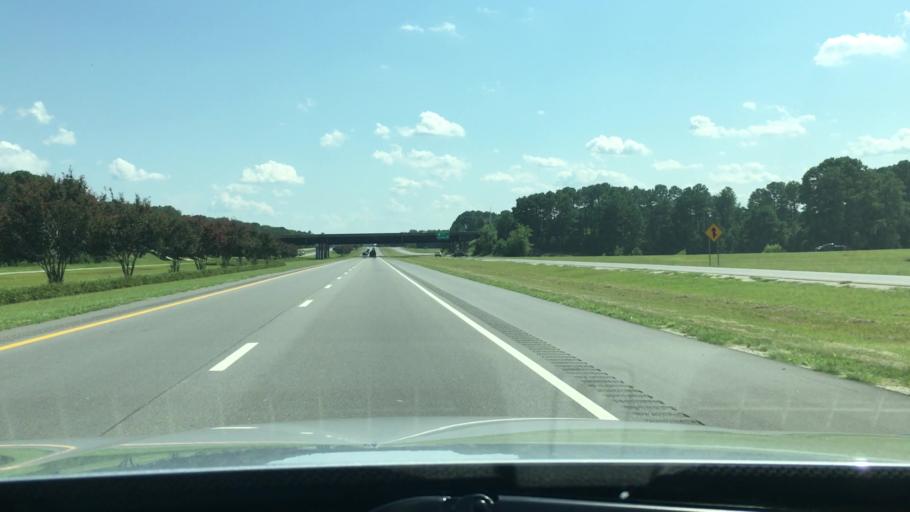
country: US
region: North Carolina
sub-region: Cumberland County
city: Vander
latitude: 35.0459
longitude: -78.8027
